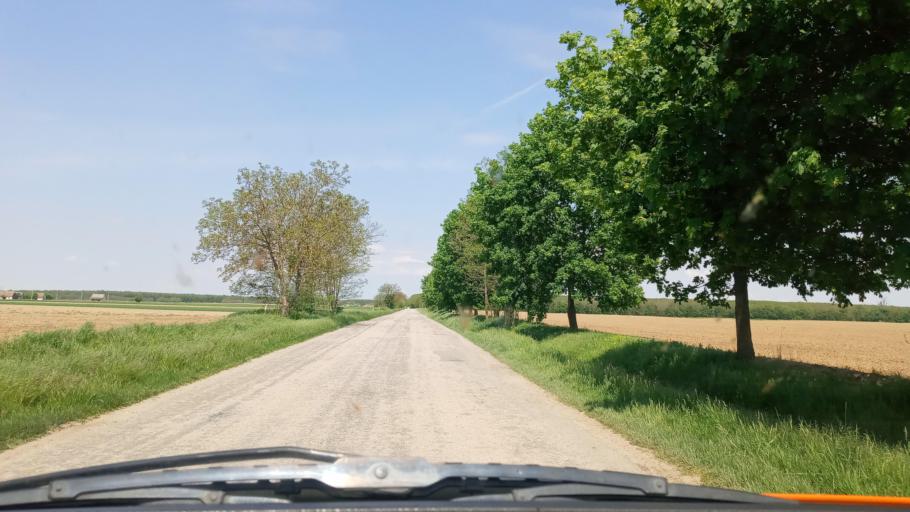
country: HU
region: Baranya
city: Boly
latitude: 45.8766
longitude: 18.5785
